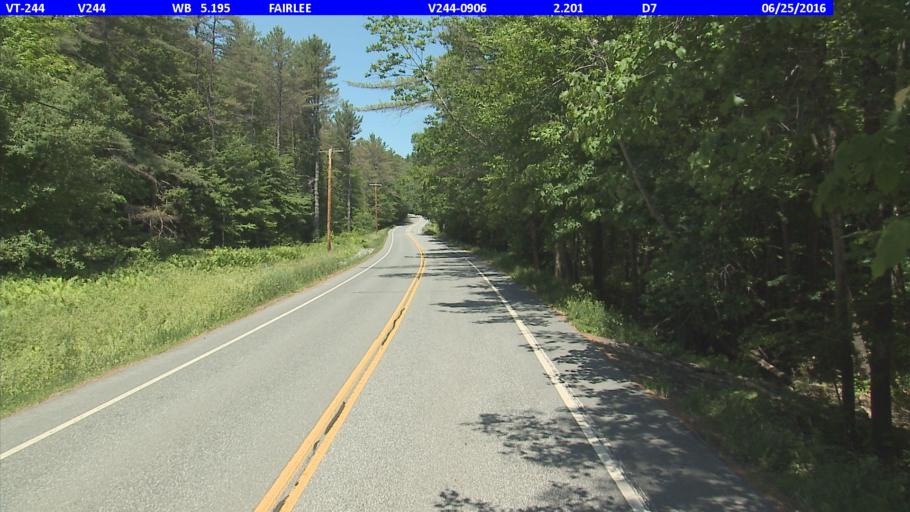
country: US
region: New Hampshire
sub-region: Grafton County
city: Orford
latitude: 43.8830
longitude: -72.1825
